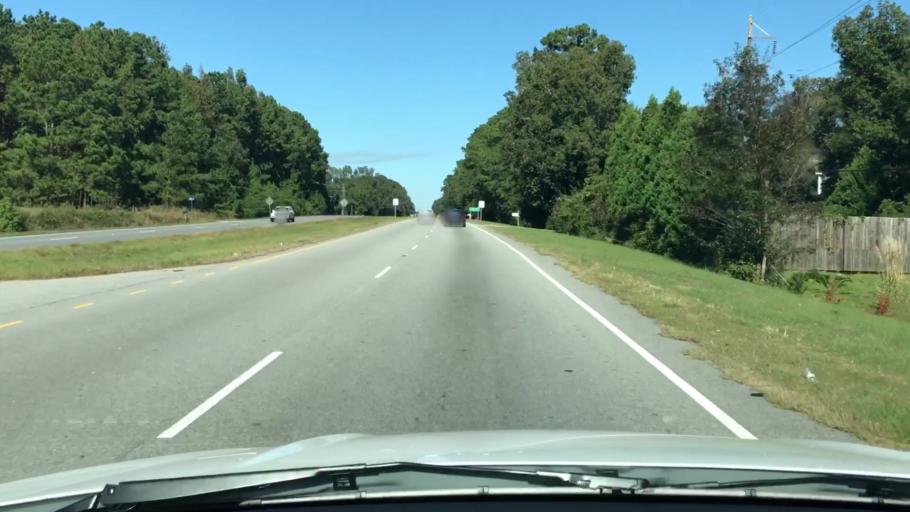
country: US
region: South Carolina
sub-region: Beaufort County
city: Laurel Bay
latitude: 32.5193
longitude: -80.7513
